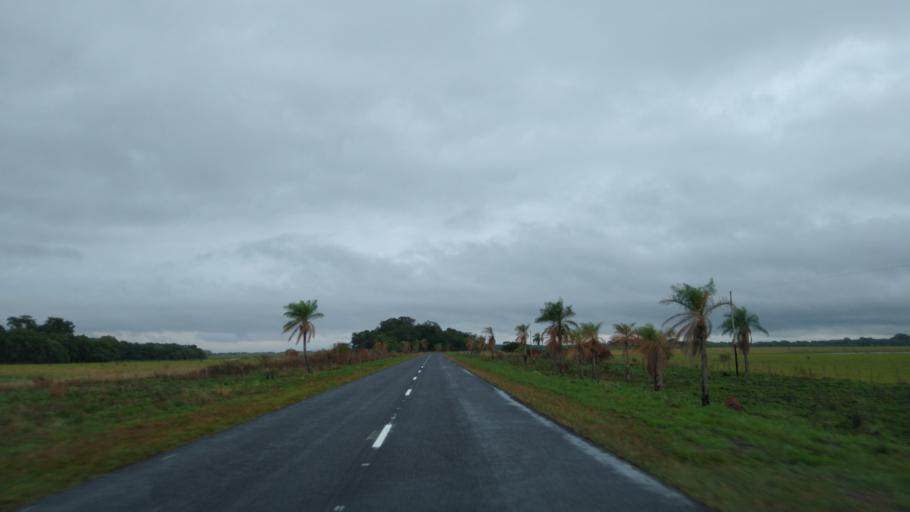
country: AR
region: Corrientes
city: Loreto
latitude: -27.6923
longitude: -57.2184
